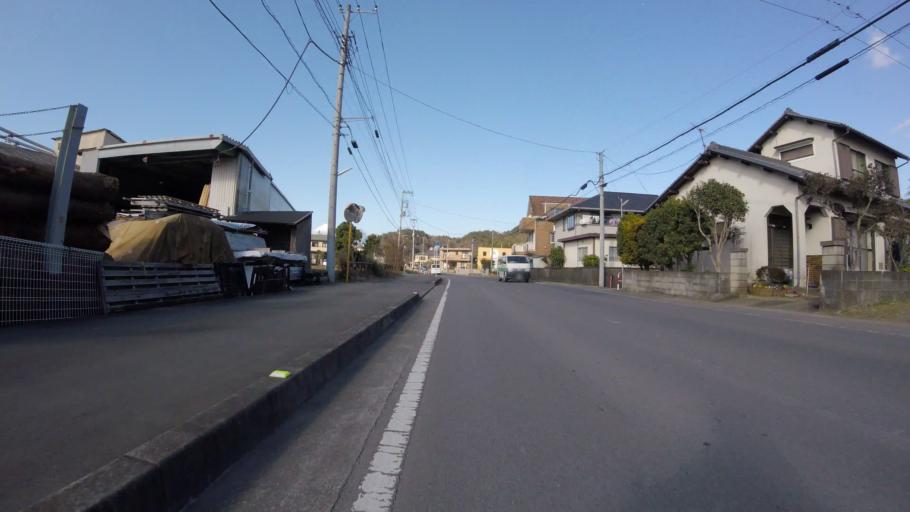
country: JP
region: Shizuoka
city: Mishima
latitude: 35.0405
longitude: 138.9584
